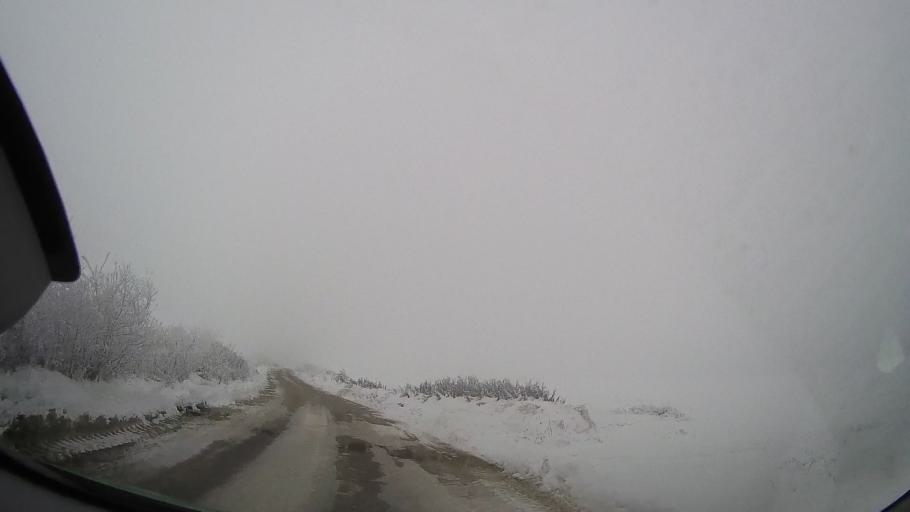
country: RO
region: Iasi
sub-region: Comuna Dagata
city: Dagata
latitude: 46.9234
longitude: 27.1732
